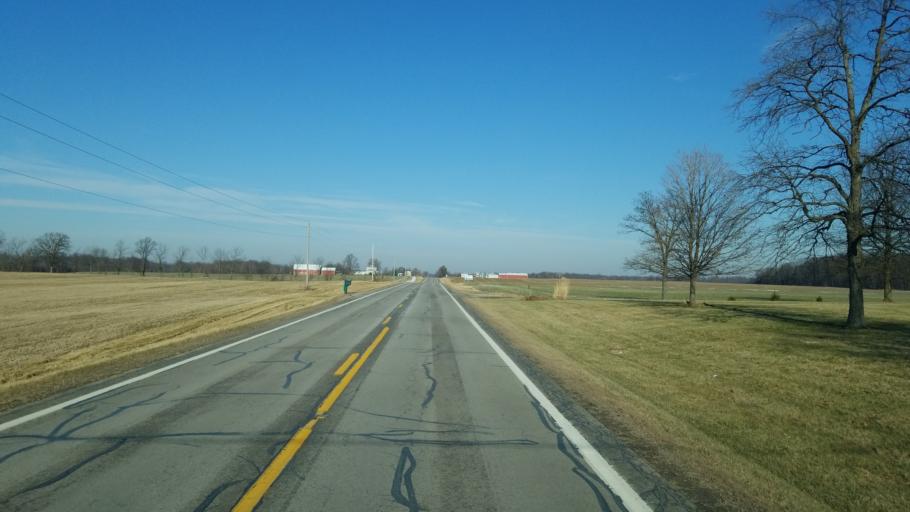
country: US
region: Ohio
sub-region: Huron County
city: Norwalk
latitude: 41.1459
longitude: -82.6537
